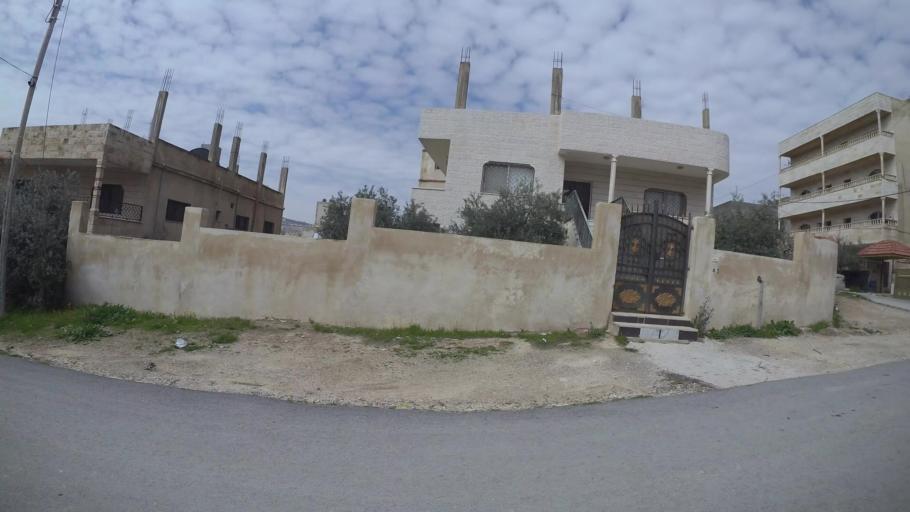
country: JO
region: Amman
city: Al Jubayhah
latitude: 32.0647
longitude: 35.8335
